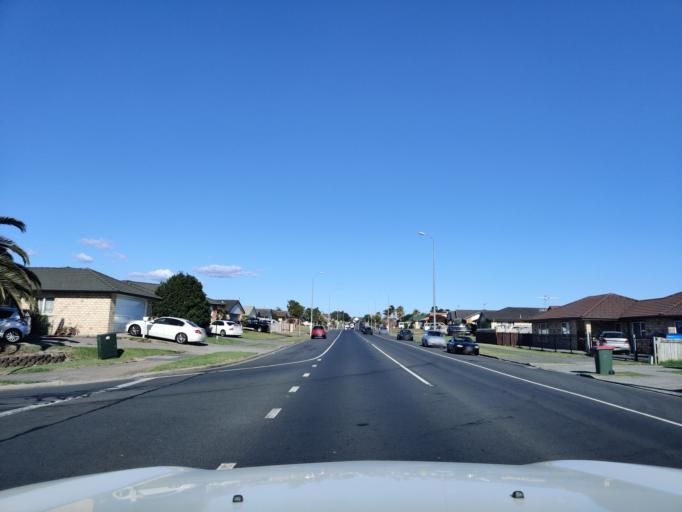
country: NZ
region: Auckland
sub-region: Auckland
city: Takanini
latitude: -37.0377
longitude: 174.8748
